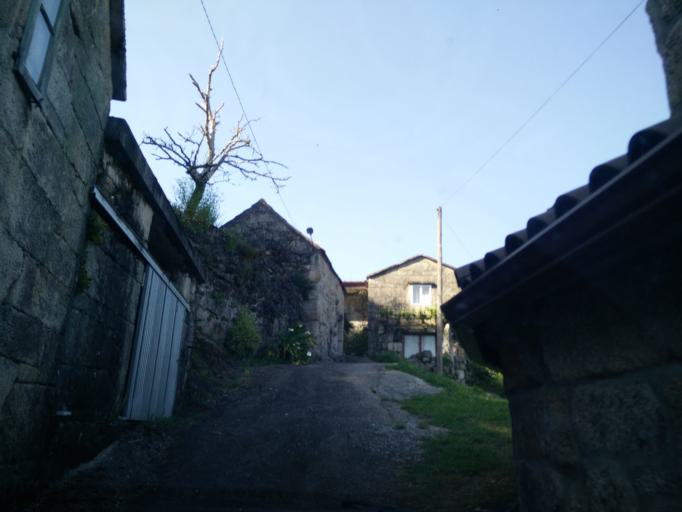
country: ES
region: Galicia
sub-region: Provincia de Pontevedra
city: Mondariz
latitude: 42.2710
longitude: -8.4074
